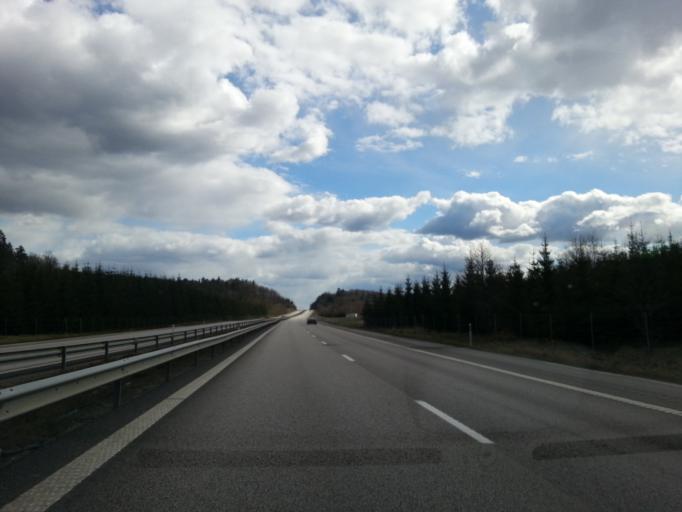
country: SE
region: Vaestra Goetaland
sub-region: Uddevalla Kommun
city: Ljungskile
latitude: 58.2670
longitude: 11.8941
